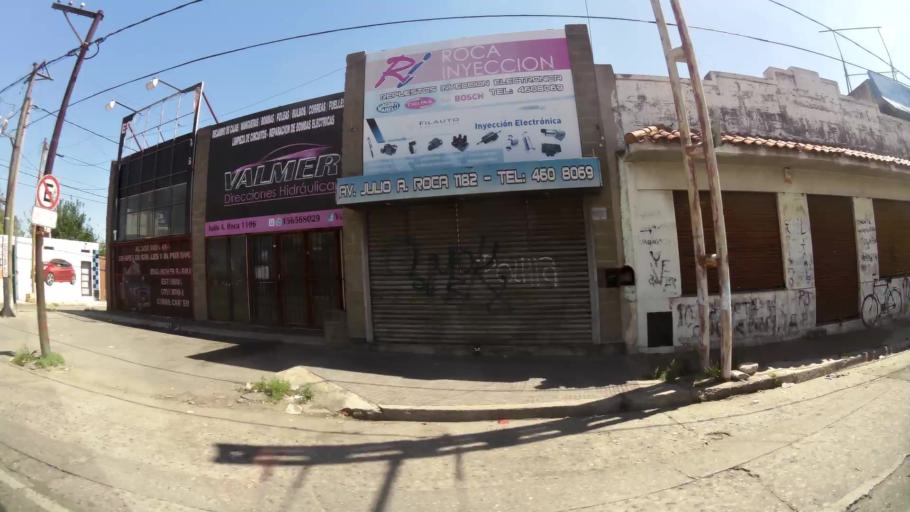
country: AR
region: Cordoba
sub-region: Departamento de Capital
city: Cordoba
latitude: -31.4277
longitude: -64.2079
